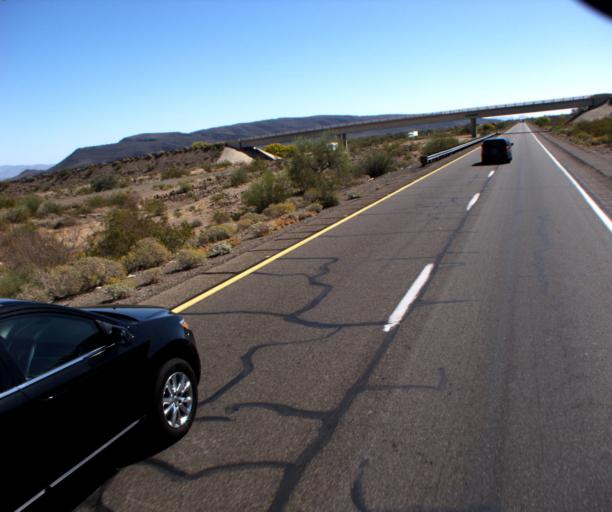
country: US
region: Arizona
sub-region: La Paz County
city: Quartzsite
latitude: 33.6562
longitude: -113.9674
